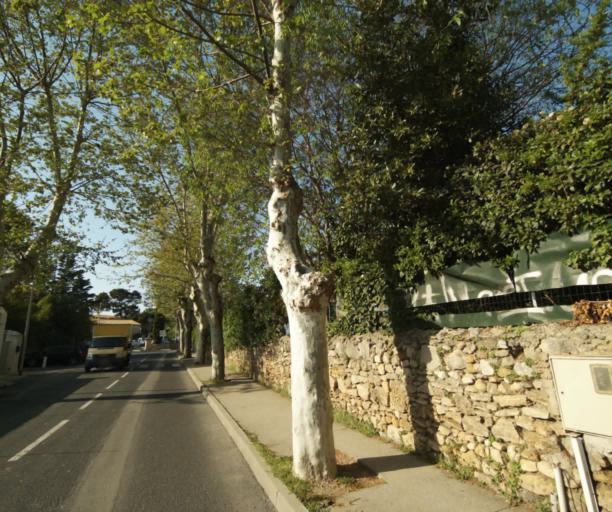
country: FR
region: Languedoc-Roussillon
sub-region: Departement de l'Herault
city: Juvignac
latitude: 43.6087
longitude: 3.7831
